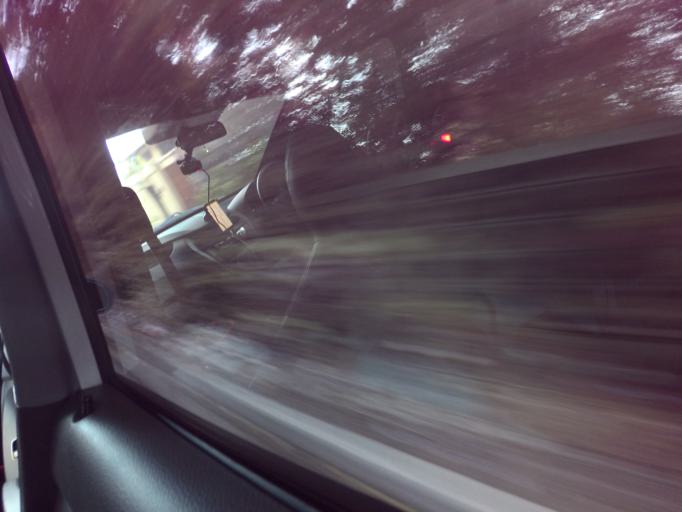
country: PH
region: Metro Manila
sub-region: San Juan
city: San Juan
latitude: 14.6060
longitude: 121.0163
